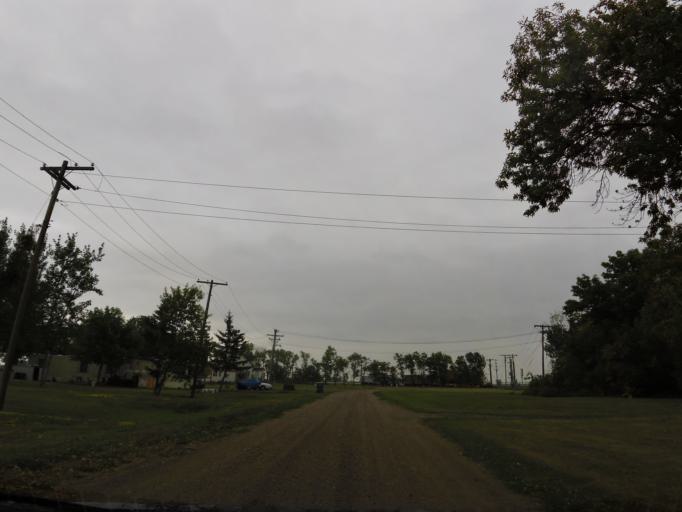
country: US
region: Minnesota
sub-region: Marshall County
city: Warren
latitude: 48.4528
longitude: -96.8713
